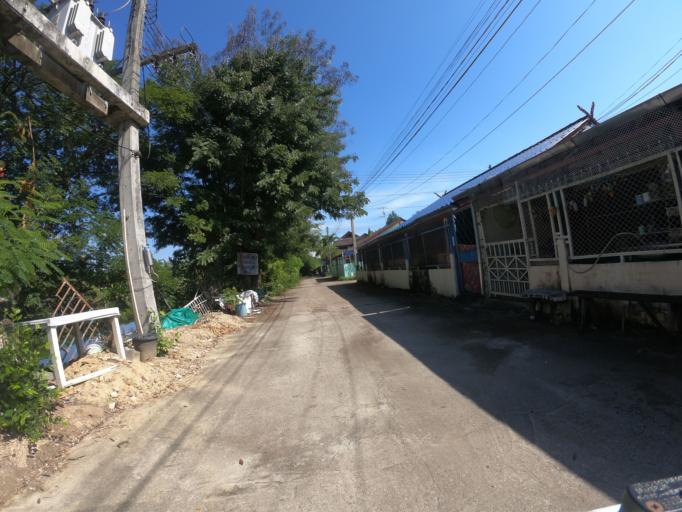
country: TH
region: Chiang Mai
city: Chiang Mai
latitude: 18.7438
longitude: 98.9736
